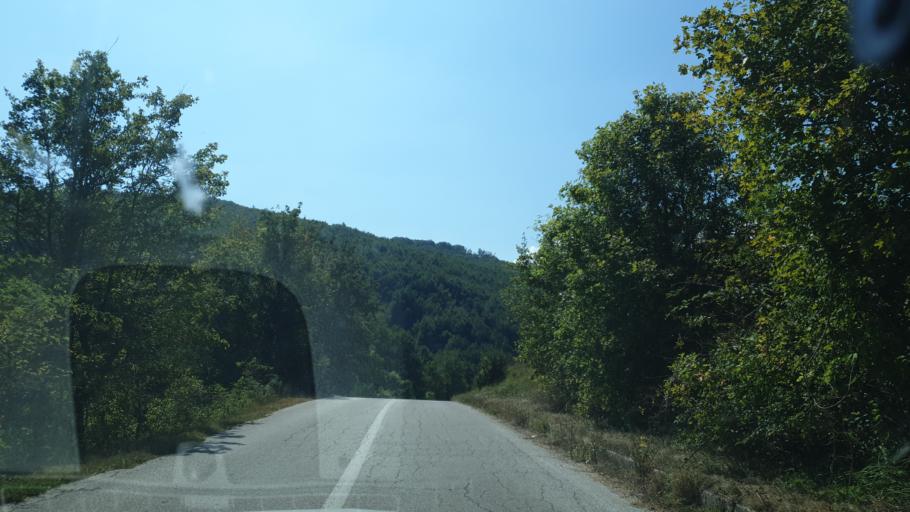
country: RS
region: Central Serbia
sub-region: Zlatiborski Okrug
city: Cajetina
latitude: 43.6824
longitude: 19.8470
